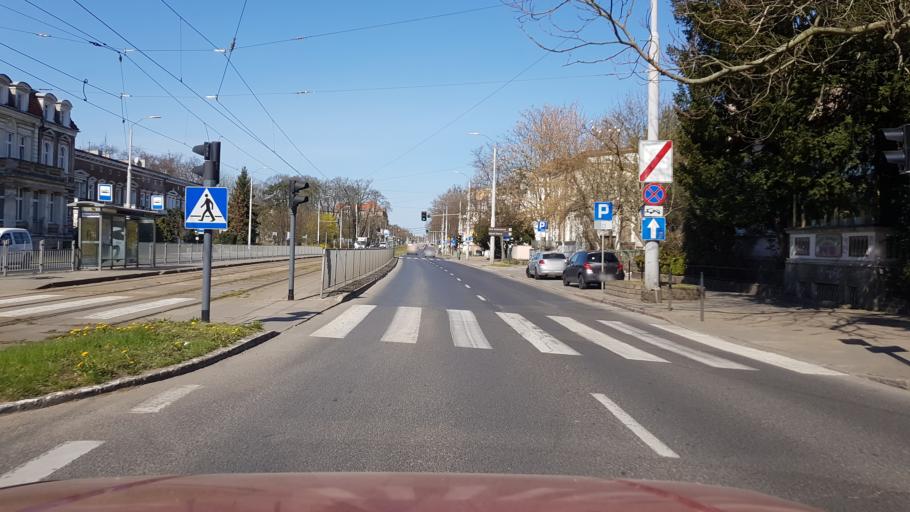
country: PL
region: West Pomeranian Voivodeship
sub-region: Szczecin
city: Szczecin
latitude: 53.4391
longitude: 14.5346
